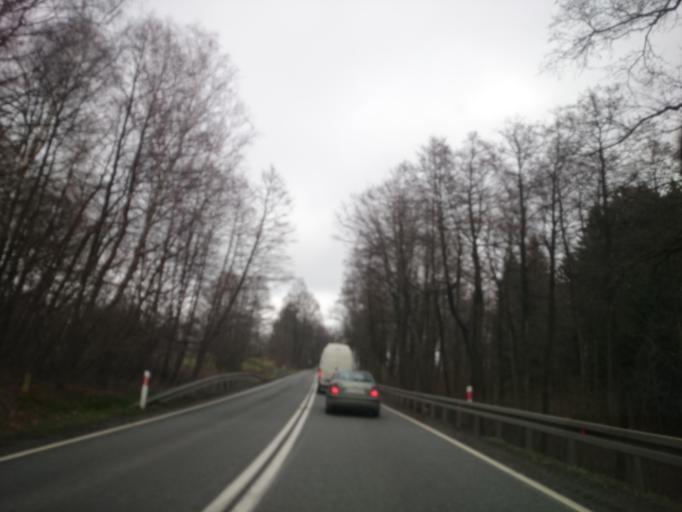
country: PL
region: Lower Silesian Voivodeship
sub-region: Powiat zabkowicki
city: Zloty Stok
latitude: 50.4347
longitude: 16.8049
